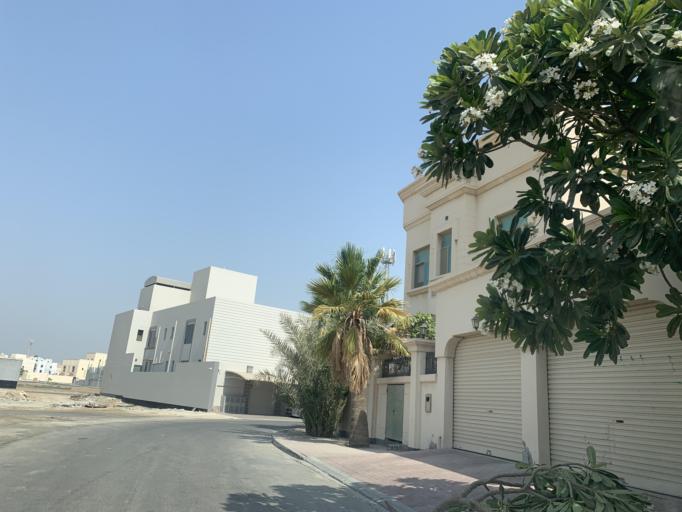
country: BH
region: Manama
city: Jidd Hafs
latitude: 26.2028
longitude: 50.5241
